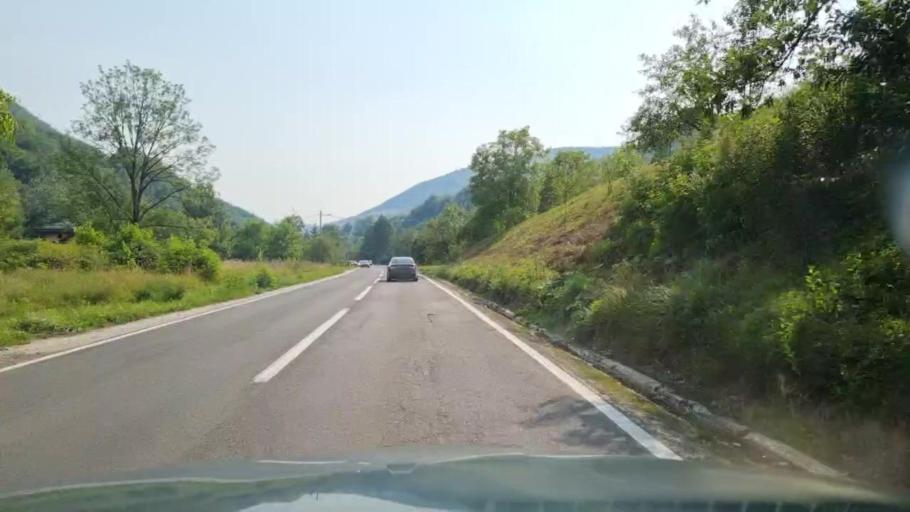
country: BA
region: Federation of Bosnia and Herzegovina
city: Vogosca
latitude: 43.9567
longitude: 18.3536
